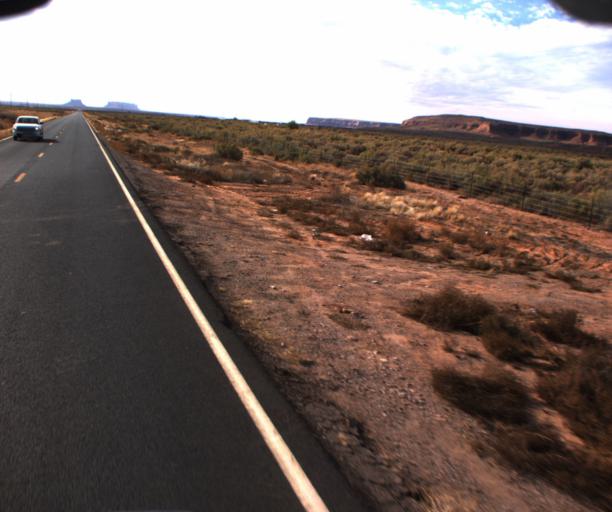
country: US
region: Arizona
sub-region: Apache County
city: Many Farms
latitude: 36.6744
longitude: -109.6005
